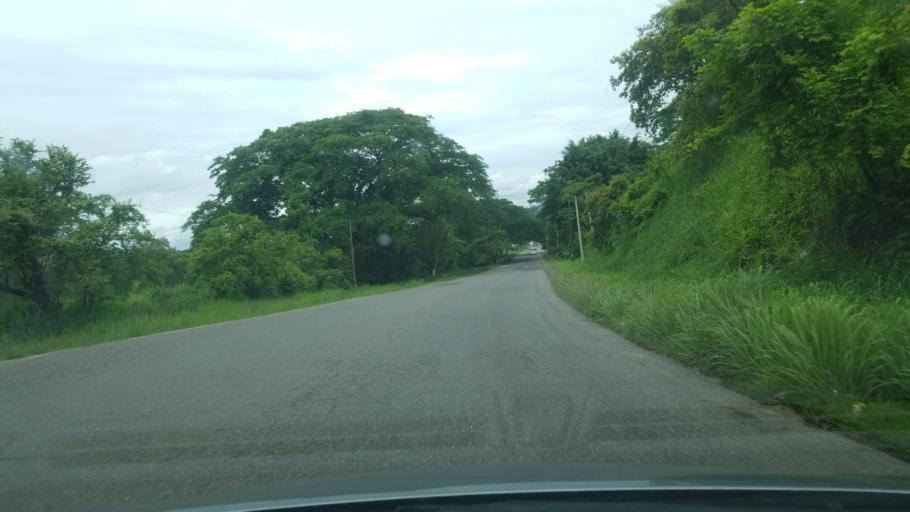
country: HN
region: Santa Barbara
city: La Flecha
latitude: 15.2959
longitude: -88.4593
